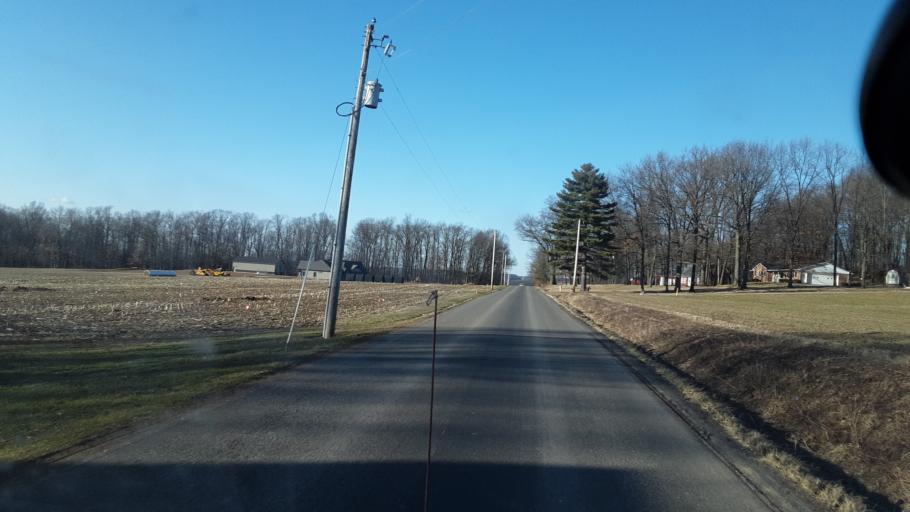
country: US
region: Ohio
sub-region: Wayne County
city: Apple Creek
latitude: 40.7160
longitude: -81.8427
